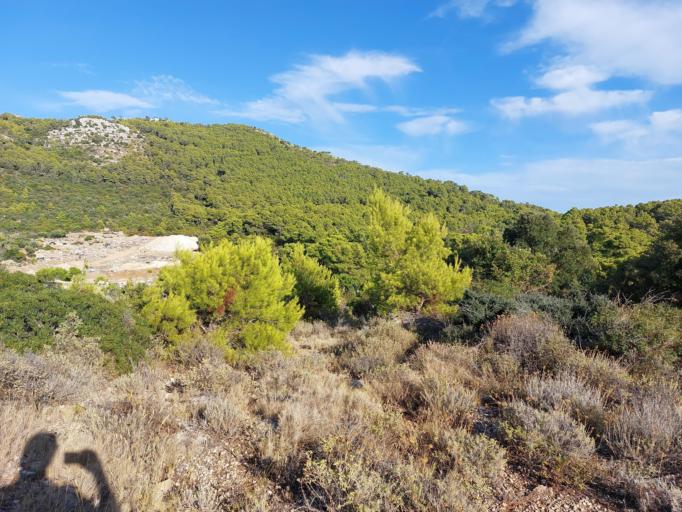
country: HR
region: Dubrovacko-Neretvanska
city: Smokvica
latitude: 42.7401
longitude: 16.8280
